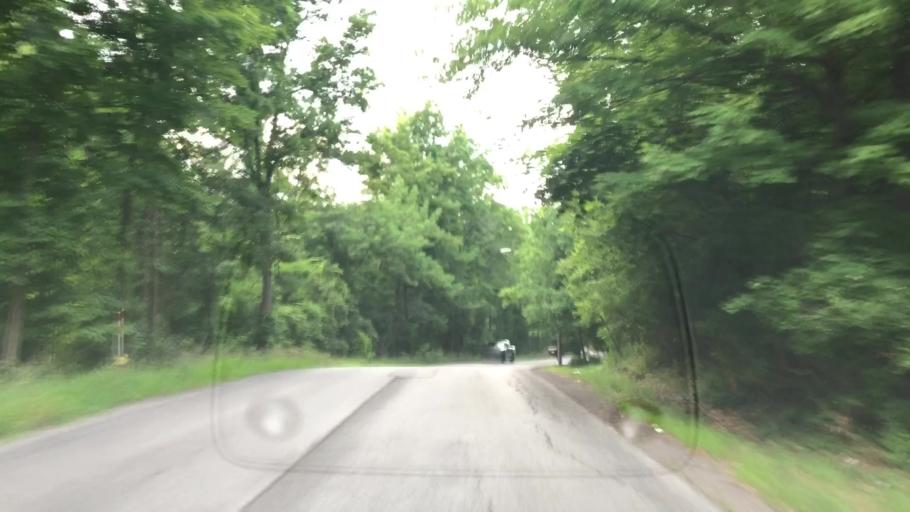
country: US
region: New York
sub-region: Erie County
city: East Aurora
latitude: 42.7828
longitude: -78.6041
